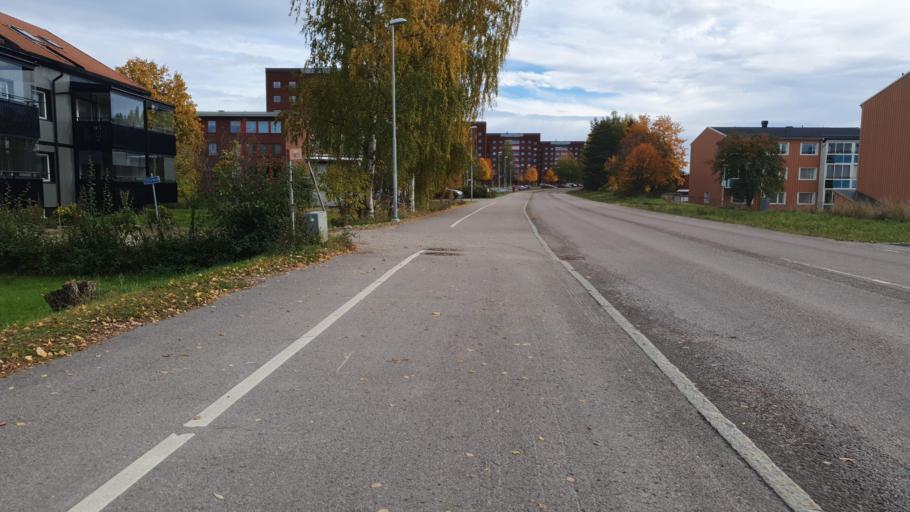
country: SE
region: Vaesternorrland
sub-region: Sundsvalls Kommun
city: Sundsvall
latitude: 62.4051
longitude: 17.2456
